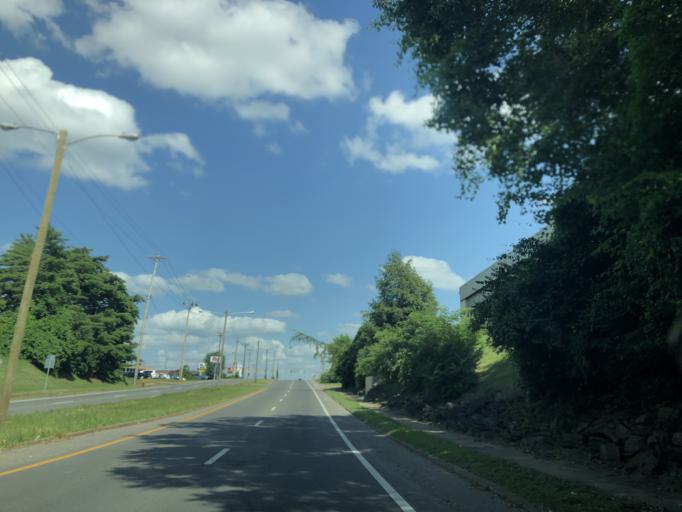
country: US
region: Tennessee
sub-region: Davidson County
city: Nashville
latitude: 36.1400
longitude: -86.7361
